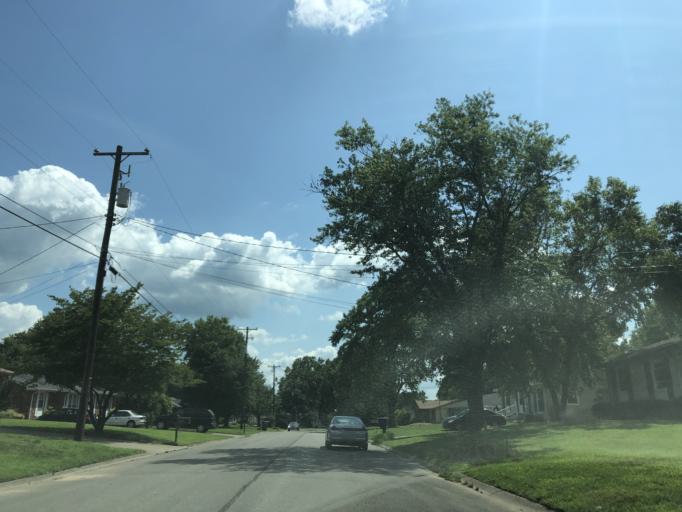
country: US
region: Tennessee
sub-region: Wilson County
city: Green Hill
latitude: 36.2225
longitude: -86.5868
